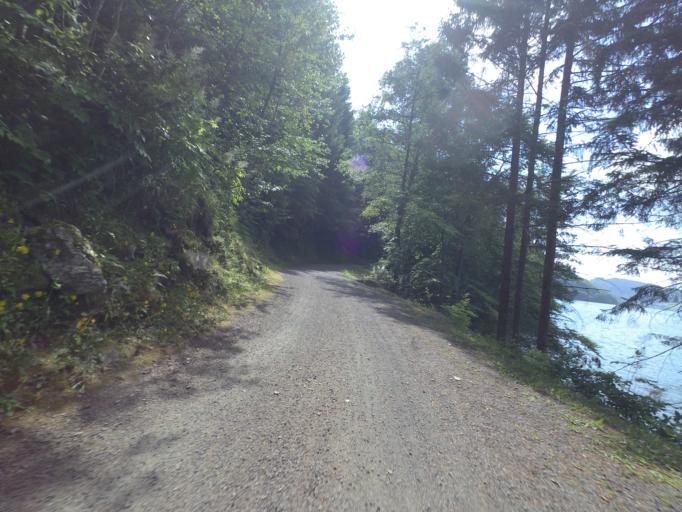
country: AT
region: Carinthia
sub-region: Politischer Bezirk Villach Land
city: Ferndorf
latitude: 46.7637
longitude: 13.6319
